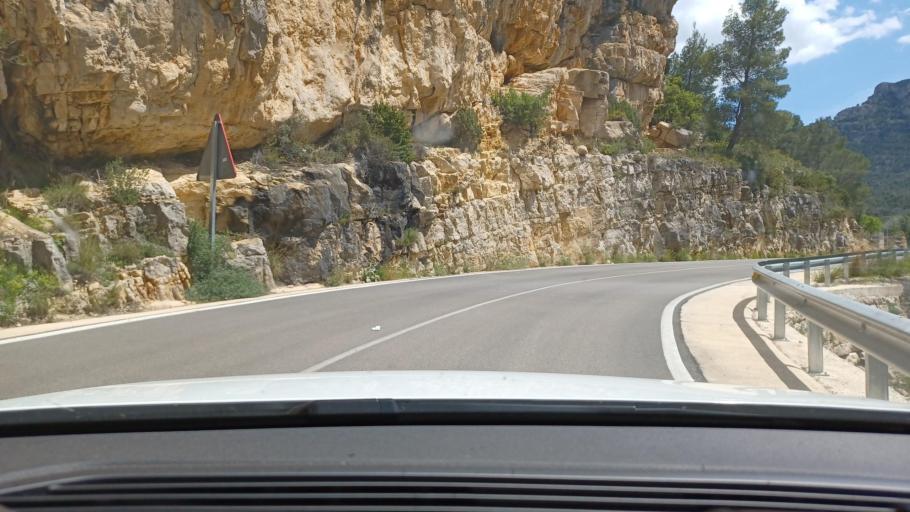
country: ES
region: Valencia
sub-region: Provincia de Castello
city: Rosell
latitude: 40.6722
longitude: 0.2383
